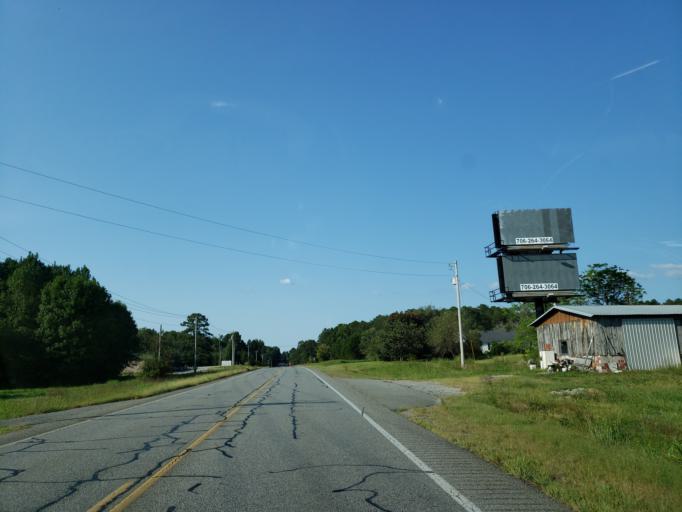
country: US
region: Tennessee
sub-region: Bradley County
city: Wildwood Lake
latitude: 34.9671
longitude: -84.7329
